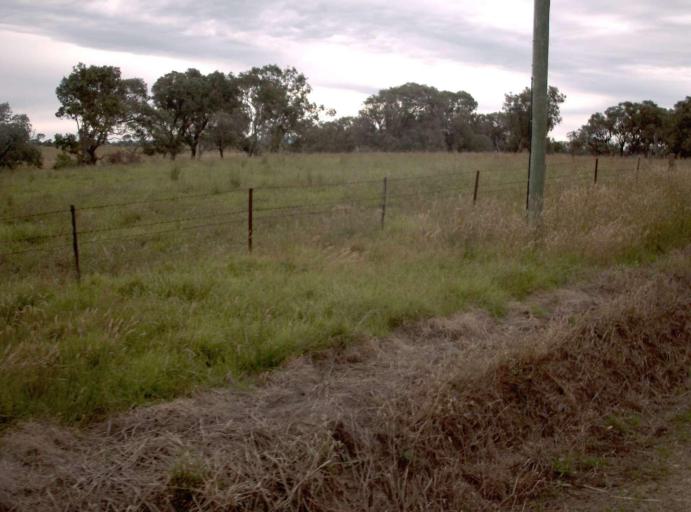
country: AU
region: Victoria
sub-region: Wellington
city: Sale
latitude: -38.0094
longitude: 147.1895
